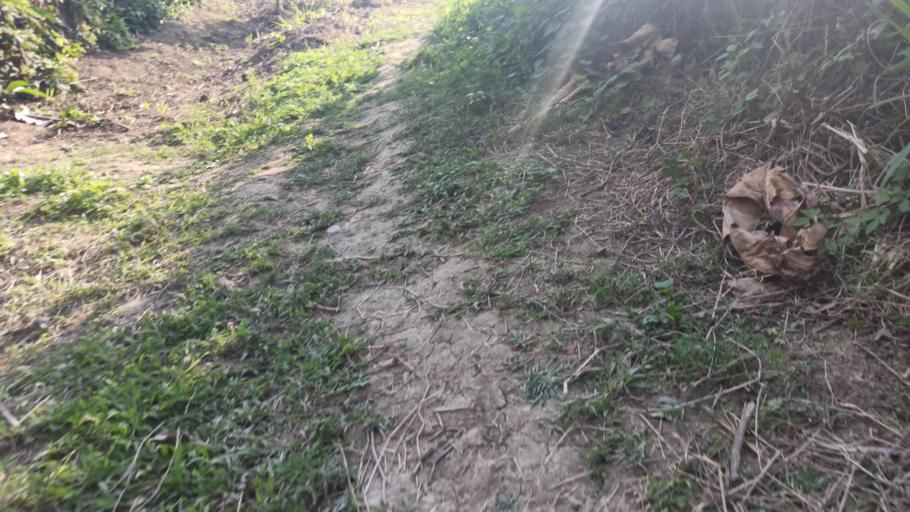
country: MX
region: Veracruz
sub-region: Poza Rica de Hidalgo
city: Arroyo del Maiz Uno
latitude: 20.4835
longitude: -97.3840
